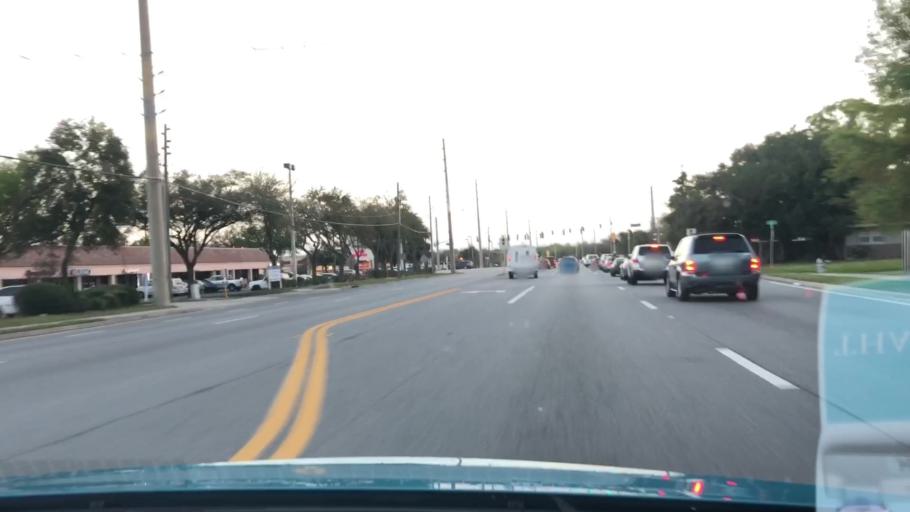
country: US
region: Florida
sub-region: Osceola County
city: Kissimmee
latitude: 28.3058
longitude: -81.3914
